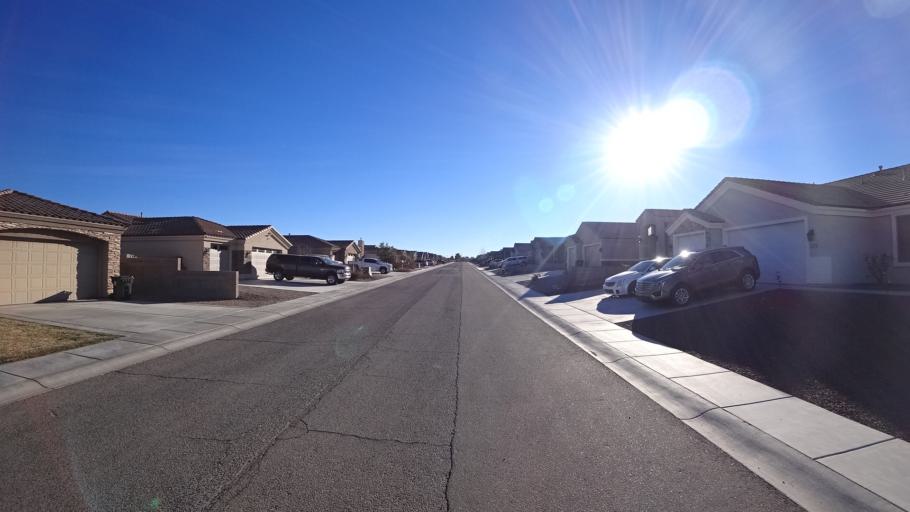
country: US
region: Arizona
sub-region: Mohave County
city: Kingman
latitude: 35.1922
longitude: -113.9981
